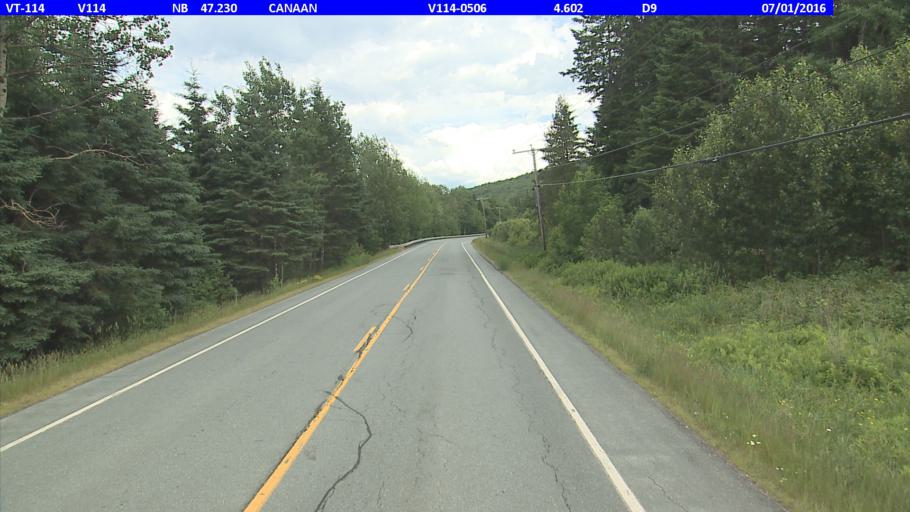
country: US
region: New Hampshire
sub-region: Coos County
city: Colebrook
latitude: 45.0072
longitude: -71.6023
